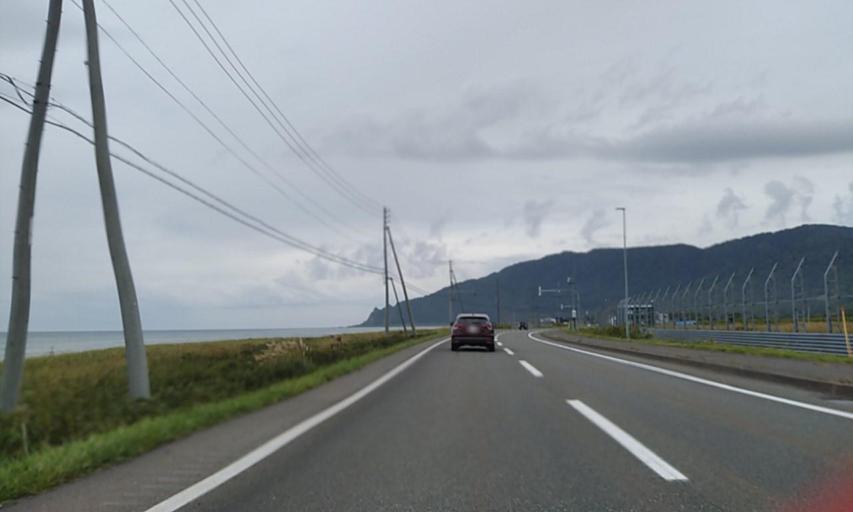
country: JP
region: Hokkaido
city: Makubetsu
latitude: 45.0821
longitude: 142.4562
